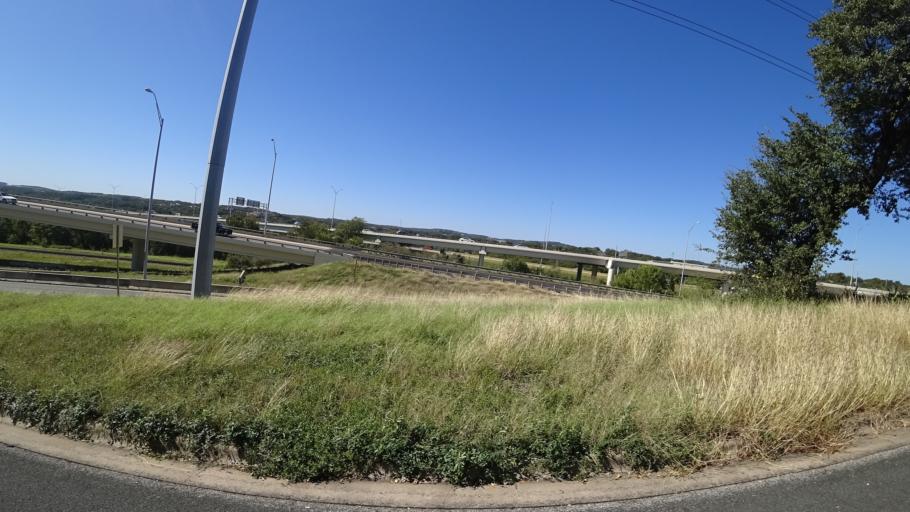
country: US
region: Texas
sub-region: Travis County
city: Rollingwood
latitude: 30.2785
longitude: -97.7668
